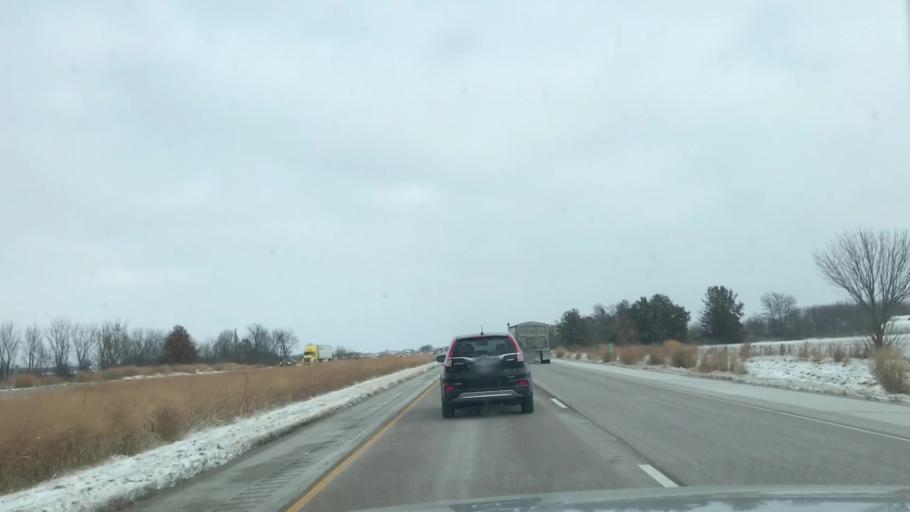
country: US
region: Illinois
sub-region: Macoupin County
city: Mount Olive
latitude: 39.1301
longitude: -89.7128
